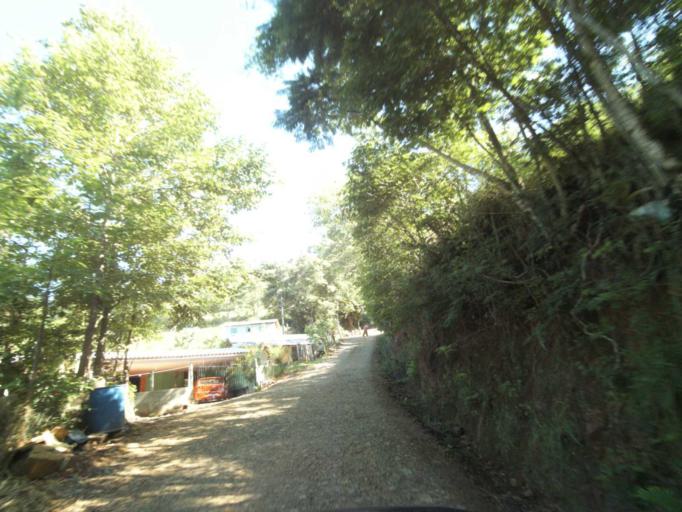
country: BR
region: Parana
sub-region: Francisco Beltrao
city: Francisco Beltrao
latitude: -26.1423
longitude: -53.3075
